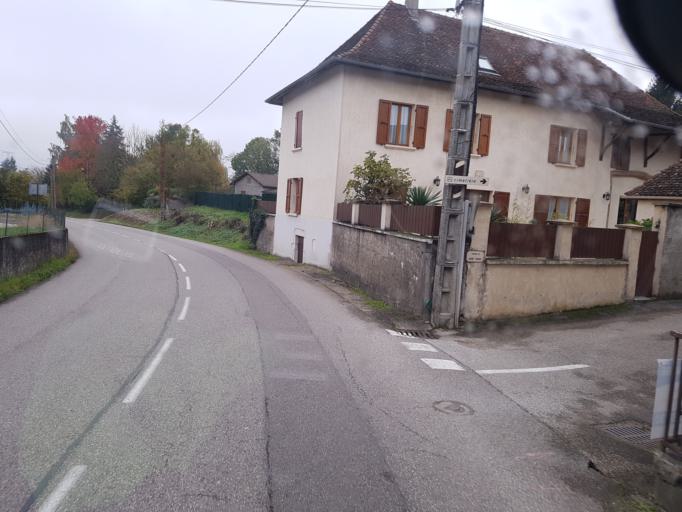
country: FR
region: Rhone-Alpes
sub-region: Departement de l'Isere
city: Aoste
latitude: 45.5882
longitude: 5.6119
